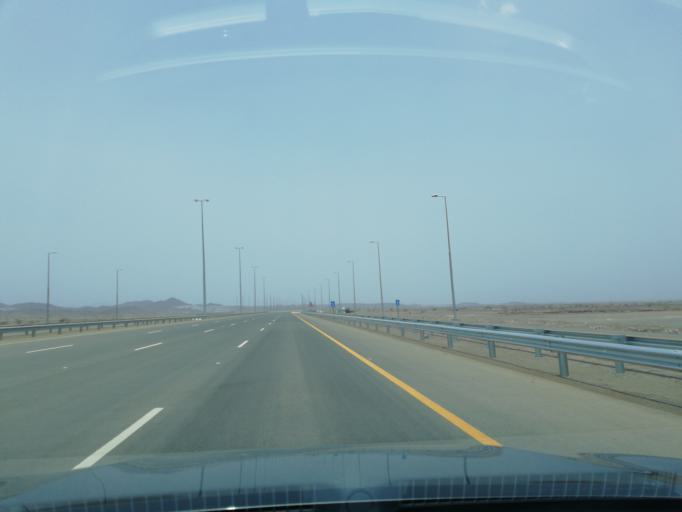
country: OM
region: Al Batinah
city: Al Liwa'
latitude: 24.4627
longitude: 56.5121
